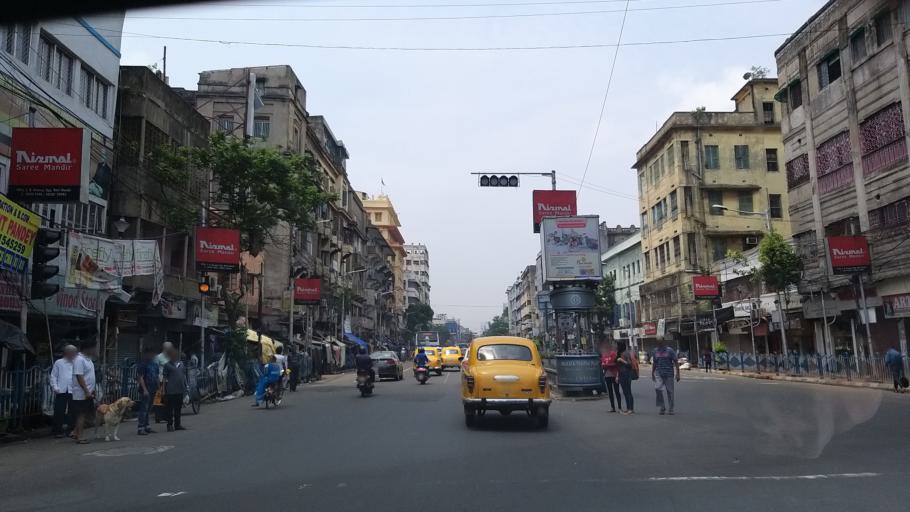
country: IN
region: West Bengal
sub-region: Kolkata
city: Bara Bazar
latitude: 22.5840
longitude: 88.3622
